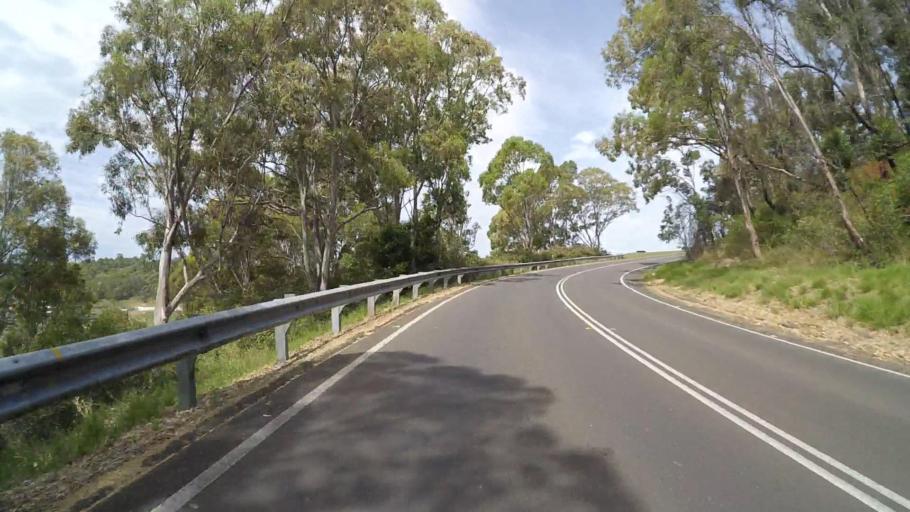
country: AU
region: New South Wales
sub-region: Shellharbour
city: Albion Park Rail
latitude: -34.5961
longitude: 150.7851
